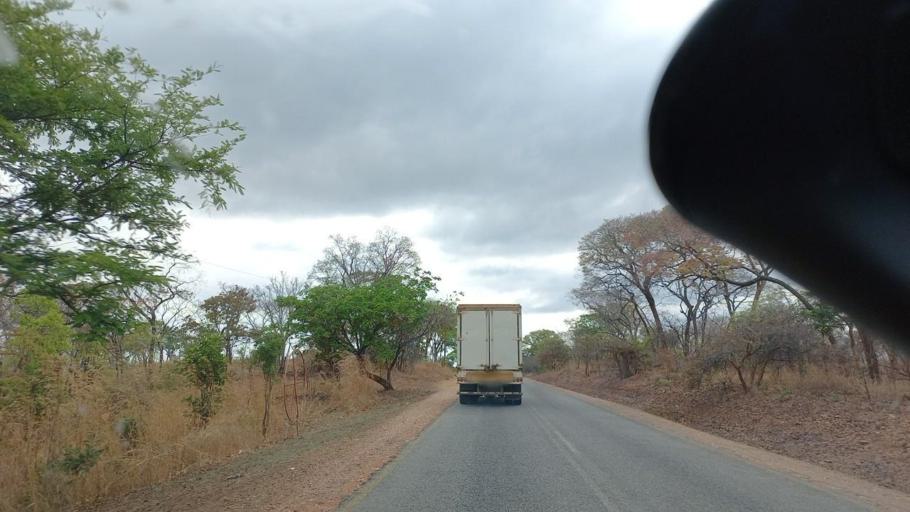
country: ZM
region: Lusaka
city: Chongwe
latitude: -15.1307
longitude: 29.5253
